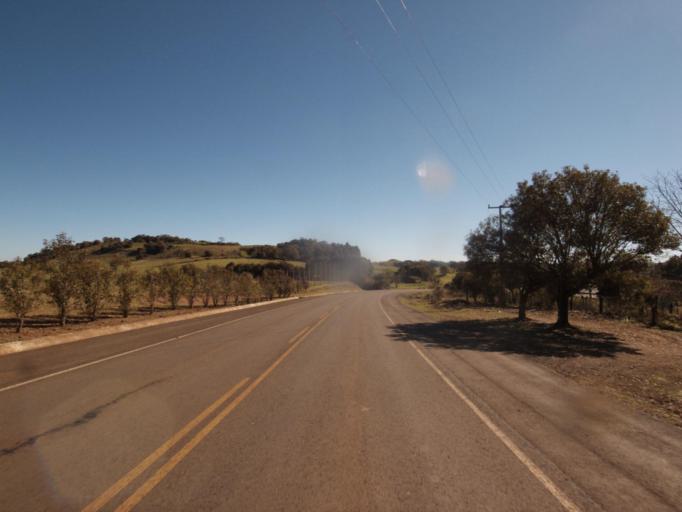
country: AR
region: Misiones
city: Bernardo de Irigoyen
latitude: -26.6394
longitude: -53.6311
